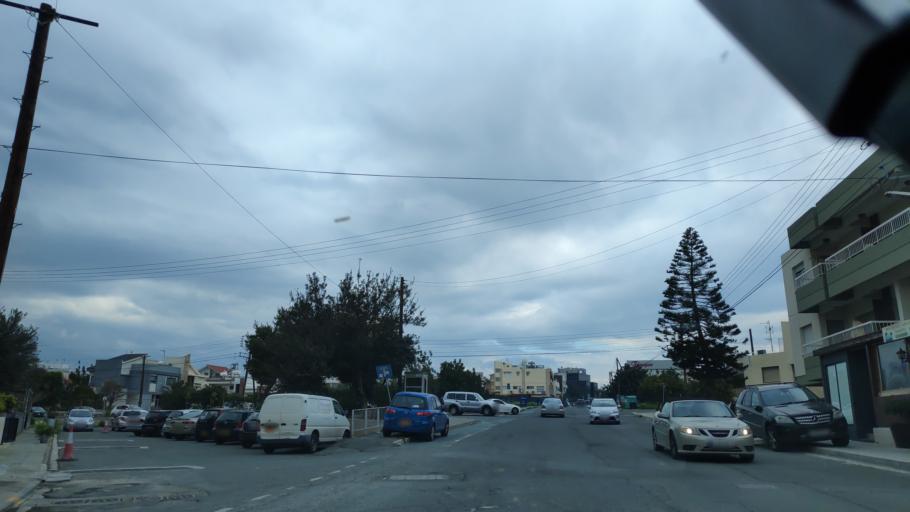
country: CY
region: Limassol
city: Limassol
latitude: 34.6946
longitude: 33.0218
